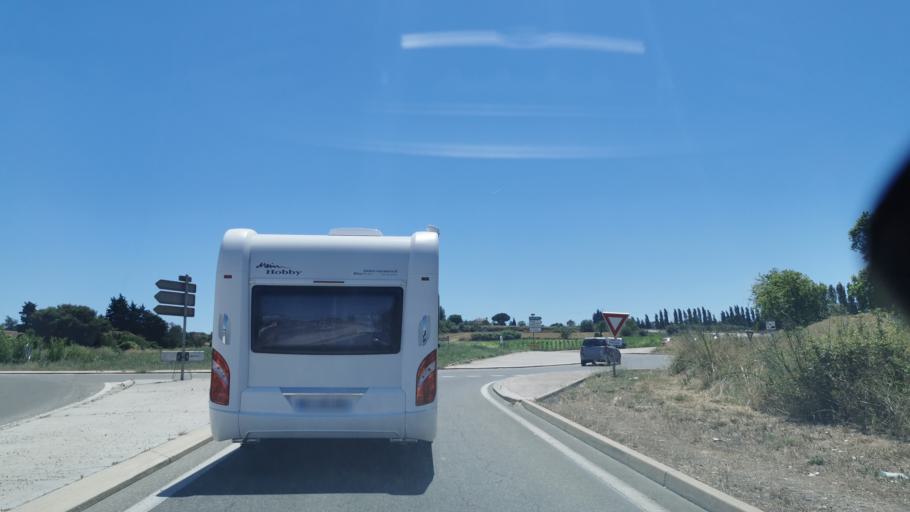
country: FR
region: Languedoc-Roussillon
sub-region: Departement de l'Herault
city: Beziers
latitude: 43.3234
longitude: 3.1894
